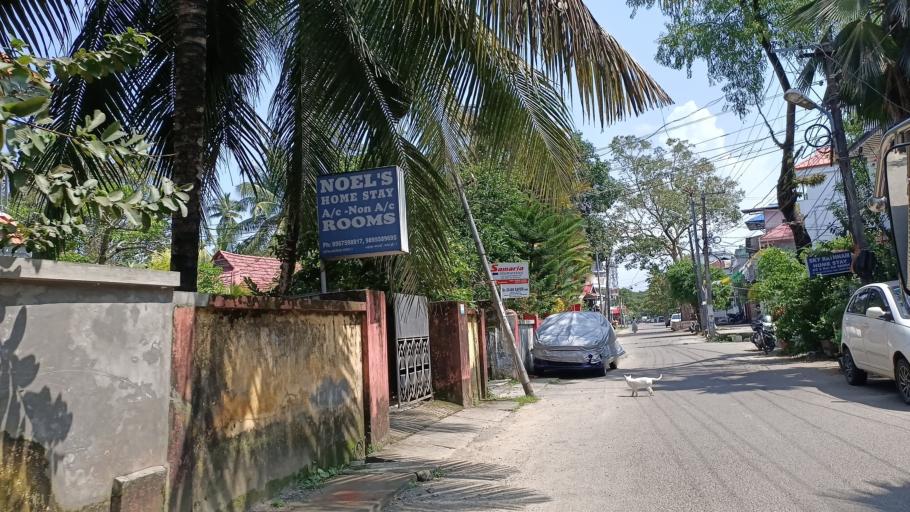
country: IN
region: Kerala
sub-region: Ernakulam
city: Cochin
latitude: 9.9607
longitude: 76.2419
